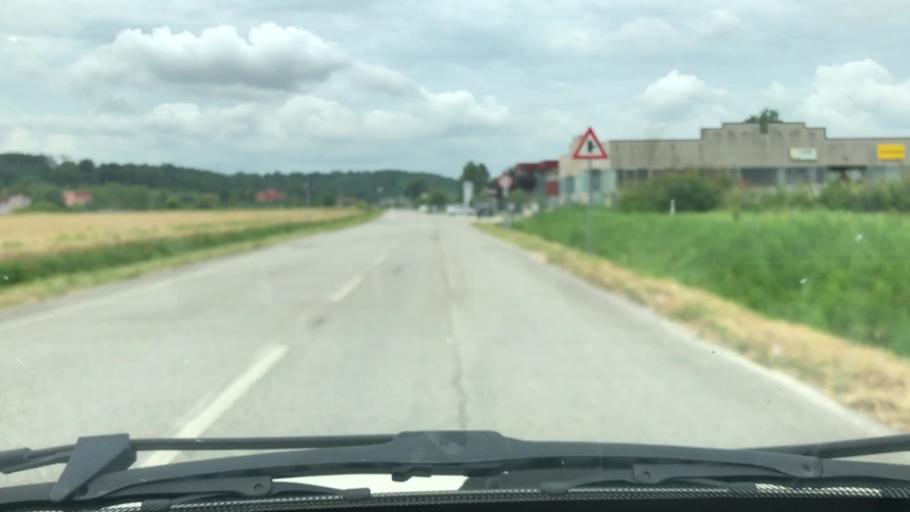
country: IT
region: Tuscany
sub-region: Province of Pisa
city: Bientina
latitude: 43.6978
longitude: 10.6244
